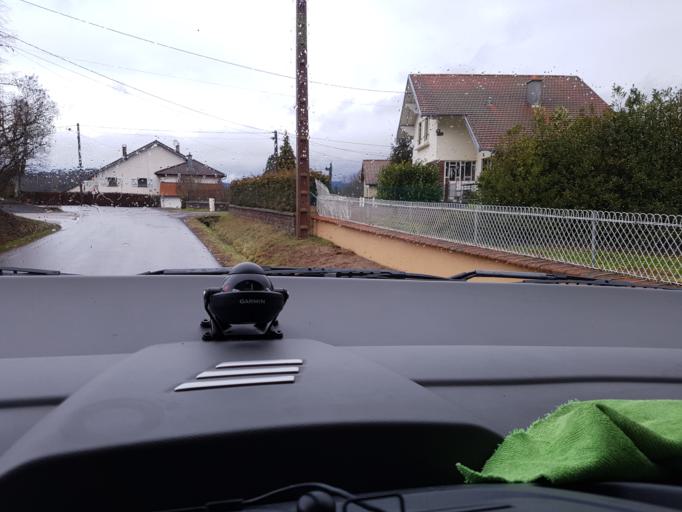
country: FR
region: Lorraine
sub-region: Departement des Vosges
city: Saint-Michel-sur-Meurthe
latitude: 48.3113
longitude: 6.8854
